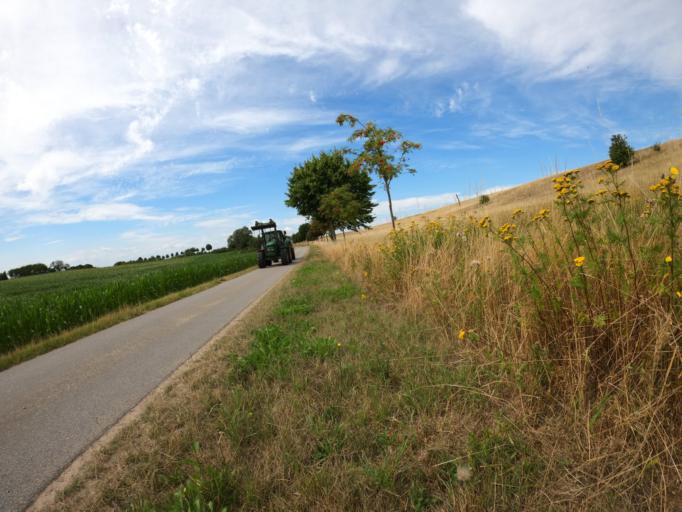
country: DE
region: Mecklenburg-Vorpommern
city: Loitz
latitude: 53.4534
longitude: 13.4806
